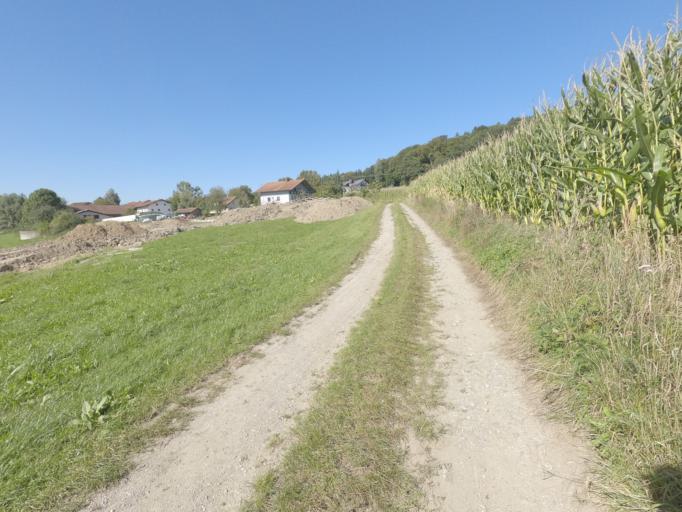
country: DE
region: Bavaria
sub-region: Lower Bavaria
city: Schaufling
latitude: 48.8210
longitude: 13.0212
